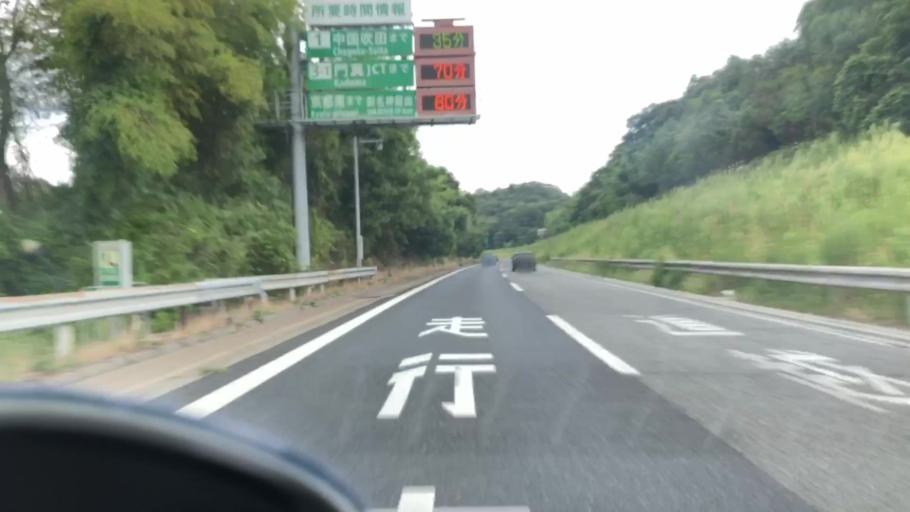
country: JP
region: Hyogo
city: Sandacho
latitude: 34.8909
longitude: 135.1269
